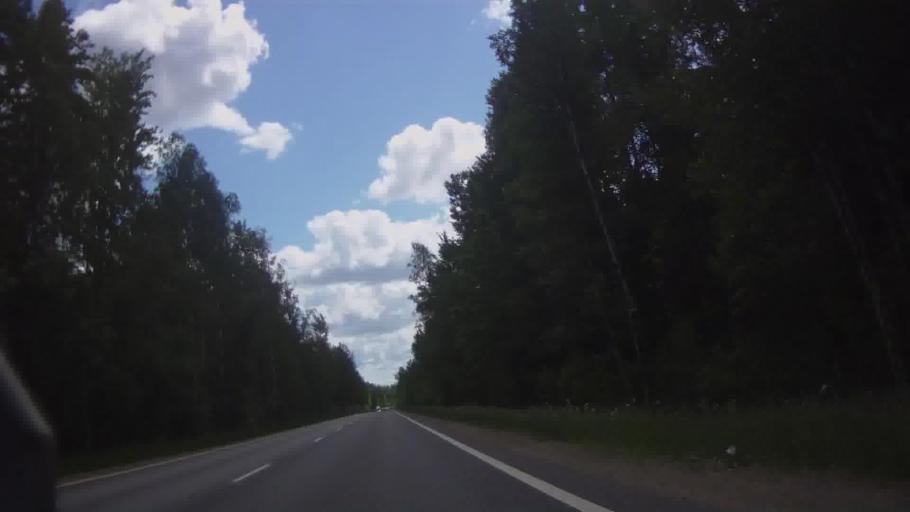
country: LV
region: Livani
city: Livani
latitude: 56.5388
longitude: 26.1307
